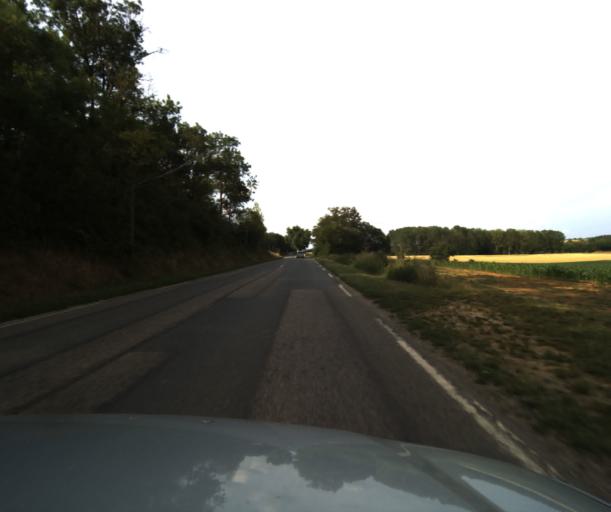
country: FR
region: Midi-Pyrenees
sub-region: Departement du Tarn-et-Garonne
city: Beaumont-de-Lomagne
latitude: 43.8144
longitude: 0.9049
